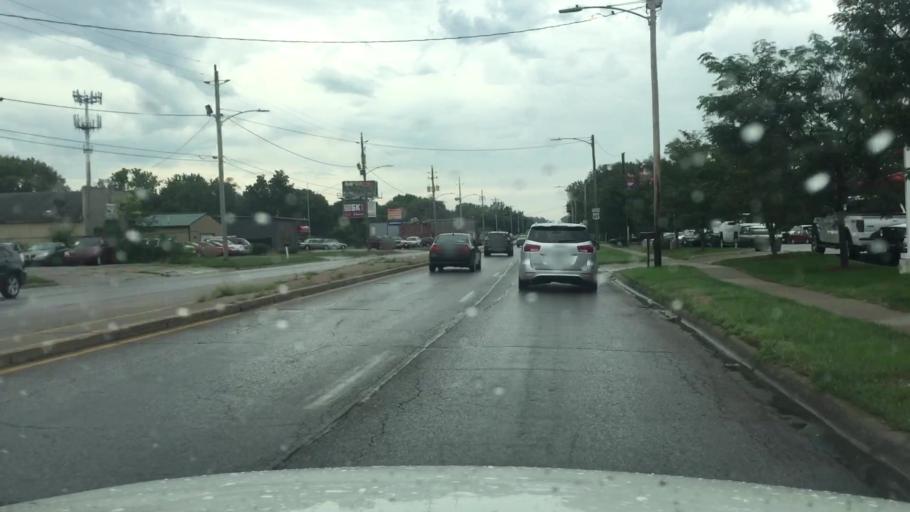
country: US
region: Iowa
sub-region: Polk County
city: Des Moines
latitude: 41.5808
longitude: -93.5970
